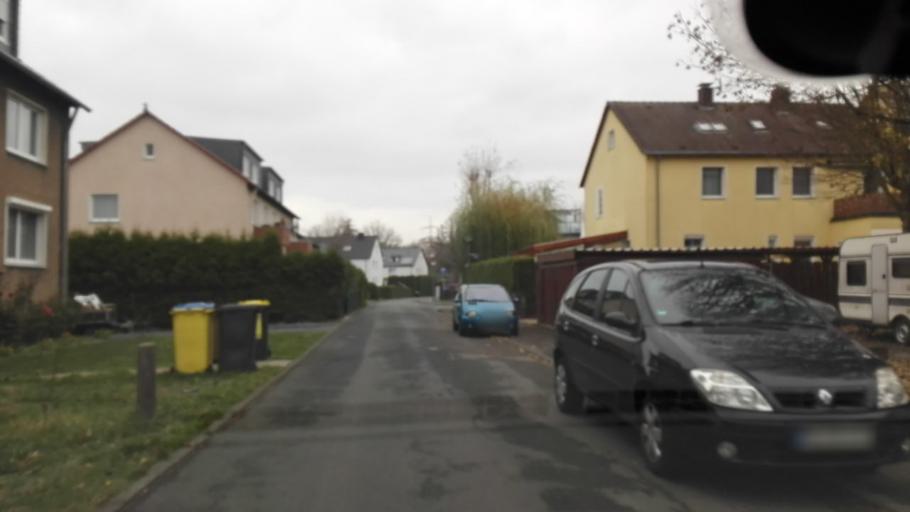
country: DE
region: North Rhine-Westphalia
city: Lanstrop
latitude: 51.5318
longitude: 7.5407
